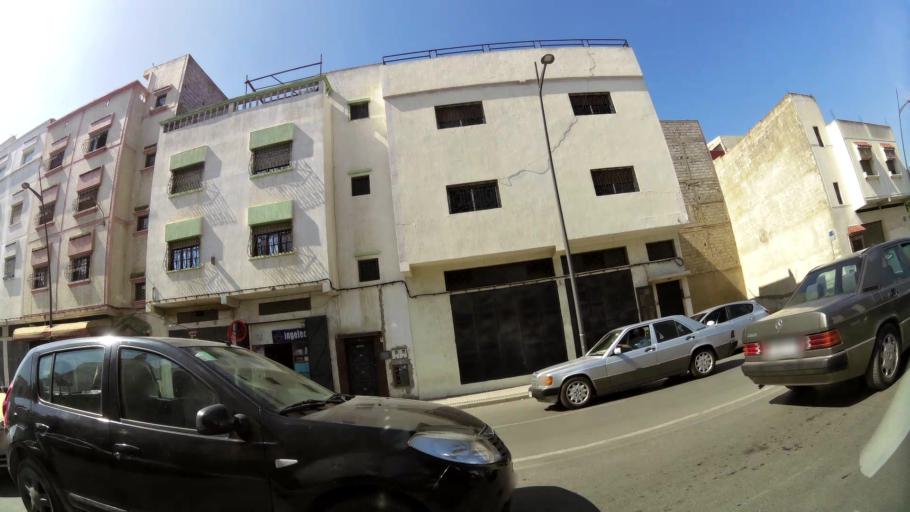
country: MA
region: Rabat-Sale-Zemmour-Zaer
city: Sale
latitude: 34.0468
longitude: -6.7747
